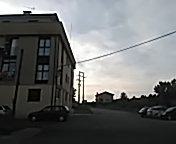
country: ES
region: Castille and Leon
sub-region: Provincia de Soria
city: San Leonardo de Yague
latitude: 41.8326
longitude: -3.0741
